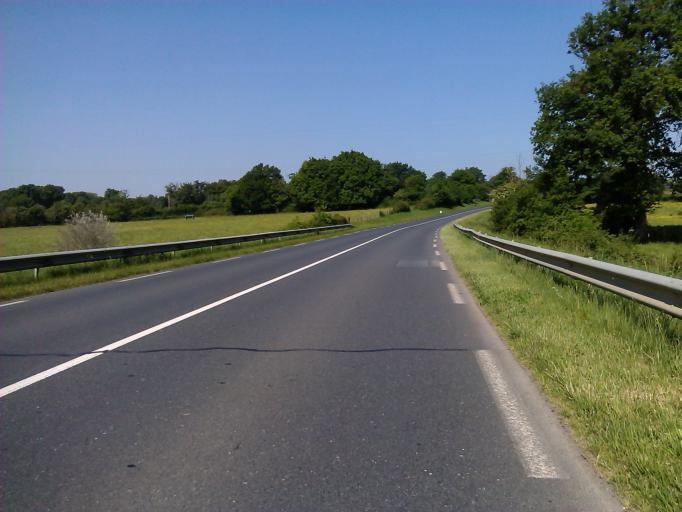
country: FR
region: Centre
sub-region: Departement de l'Indre
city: Cluis
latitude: 46.5980
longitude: 1.7338
